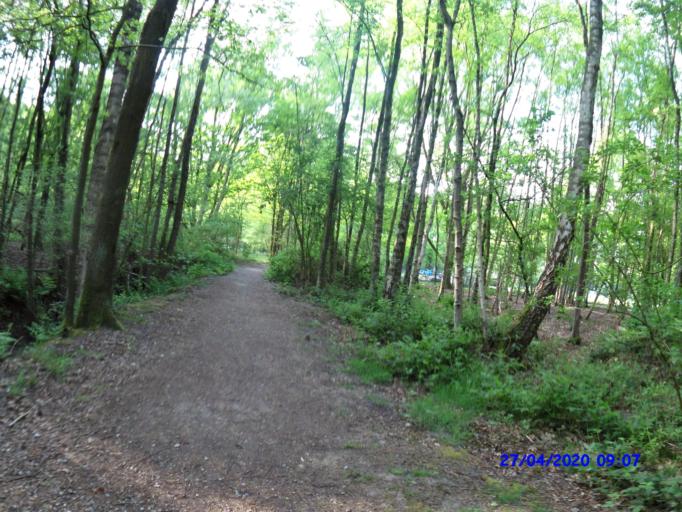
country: BE
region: Flanders
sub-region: Provincie Antwerpen
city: Turnhout
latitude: 51.3094
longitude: 4.9287
